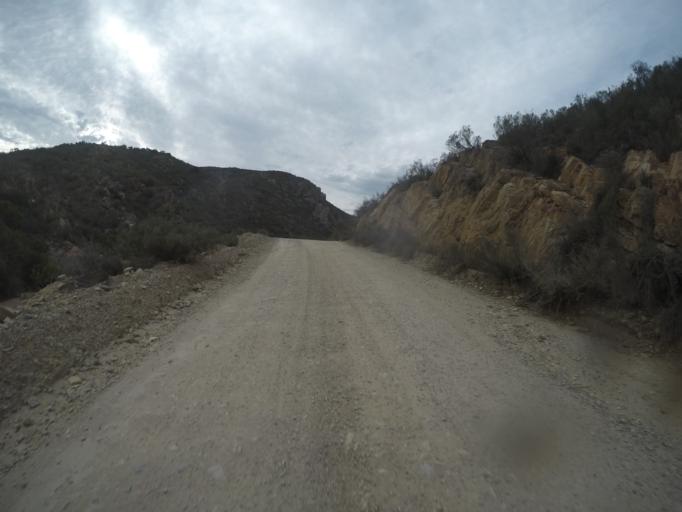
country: ZA
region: Eastern Cape
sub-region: Cacadu District Municipality
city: Willowmore
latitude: -33.5046
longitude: 23.6355
